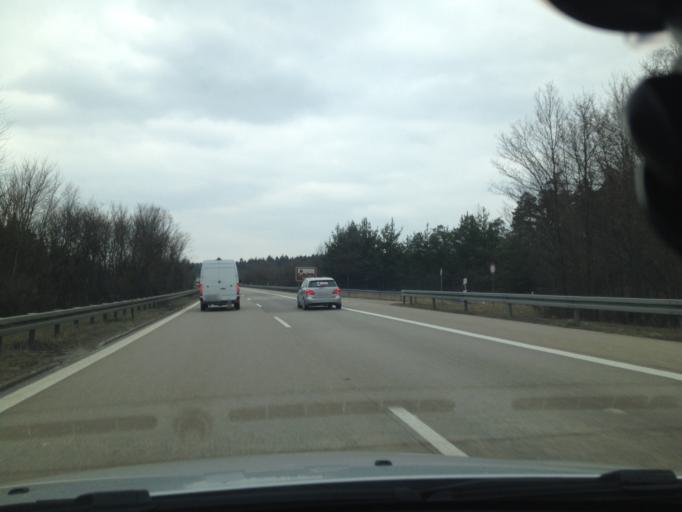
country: DE
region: Baden-Wuerttemberg
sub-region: Regierungsbezirk Stuttgart
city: Ellenberg
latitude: 49.0259
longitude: 10.1953
